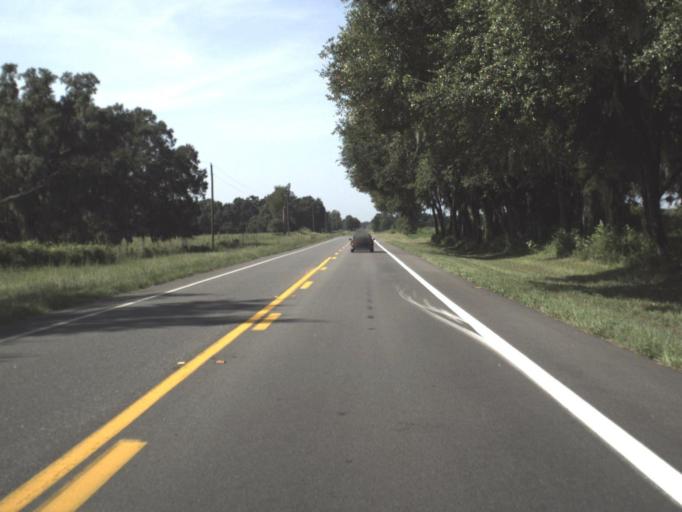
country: US
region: Florida
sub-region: Alachua County
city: High Springs
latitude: 29.9483
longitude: -82.7134
